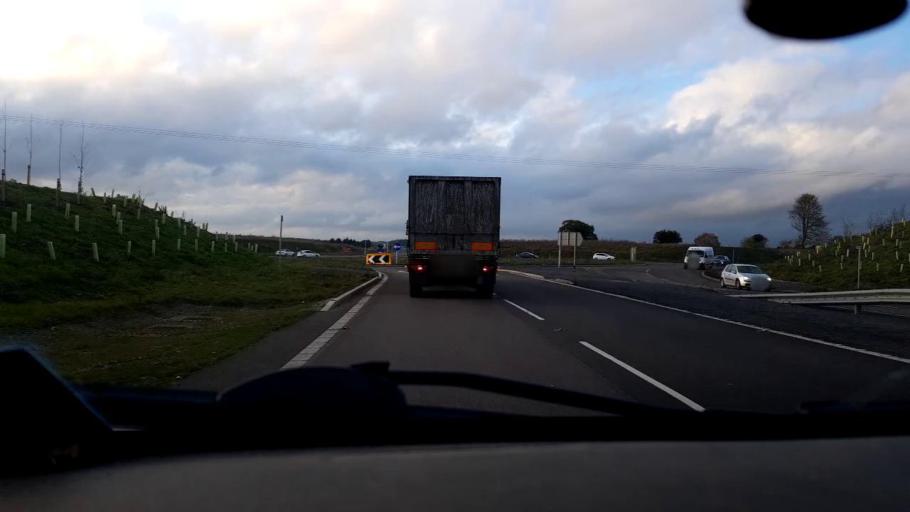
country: GB
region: England
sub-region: Norfolk
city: Horsford
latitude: 52.6861
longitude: 1.2426
